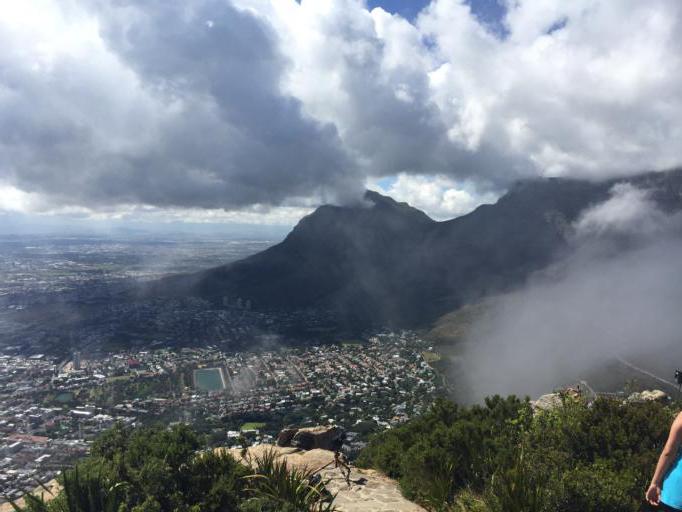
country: ZA
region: Western Cape
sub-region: City of Cape Town
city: Cape Town
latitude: -33.9350
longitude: 18.3891
